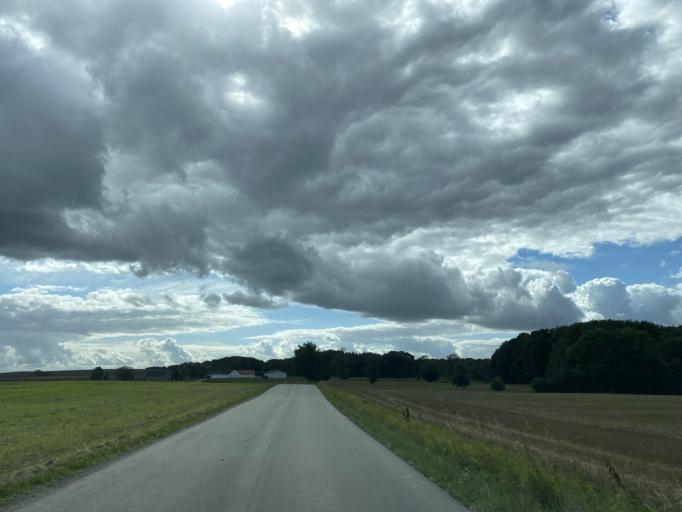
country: DK
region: Central Jutland
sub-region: Horsens Kommune
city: Horsens
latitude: 55.9623
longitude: 9.8597
